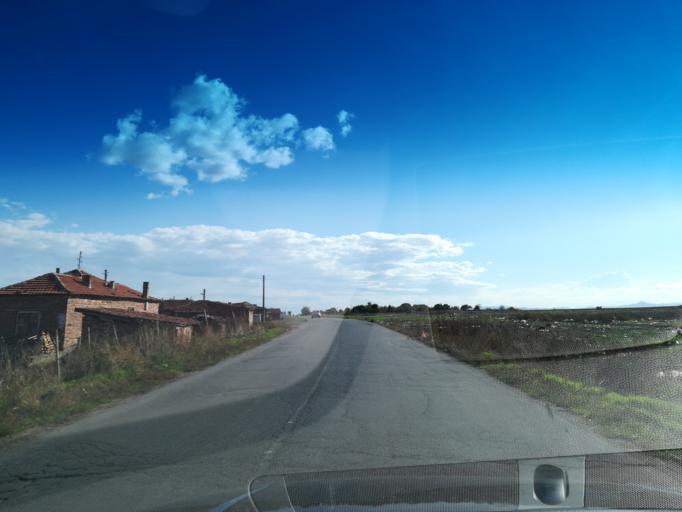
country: BG
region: Stara Zagora
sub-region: Obshtina Chirpan
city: Chirpan
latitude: 42.2026
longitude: 25.3090
